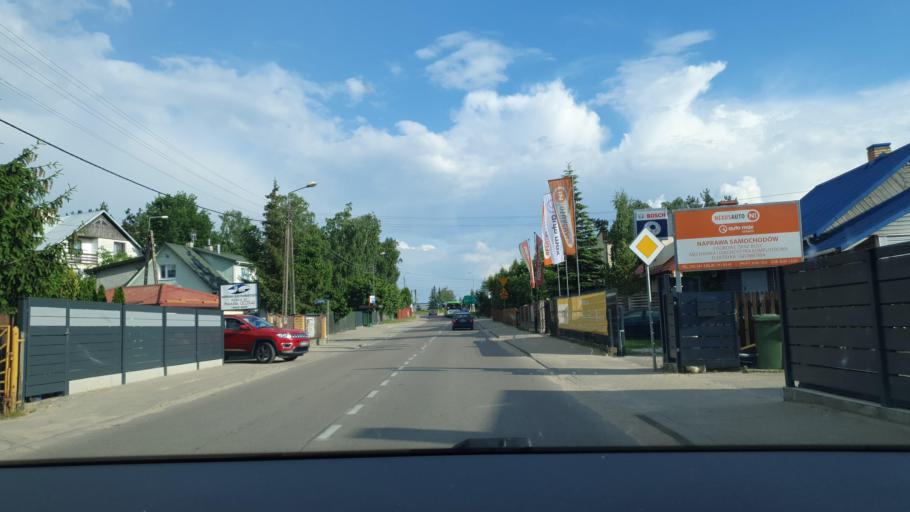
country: PL
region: Podlasie
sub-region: Powiat bialostocki
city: Wasilkow
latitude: 53.1271
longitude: 23.2580
